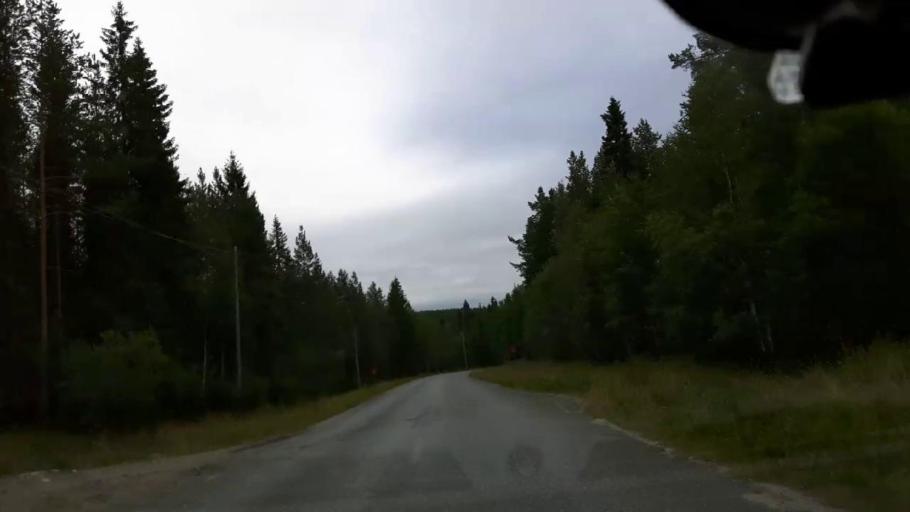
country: SE
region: Jaemtland
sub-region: Braecke Kommun
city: Braecke
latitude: 62.8876
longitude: 15.6172
